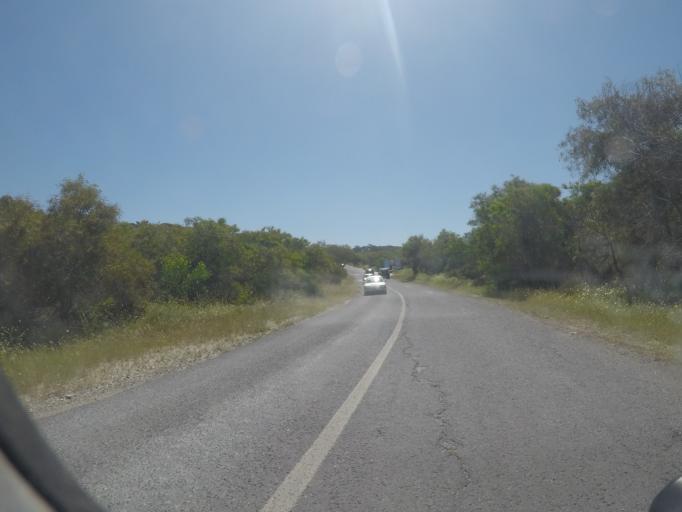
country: PT
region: Setubal
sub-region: Almada
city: Charneca
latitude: 38.6100
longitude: -9.2069
